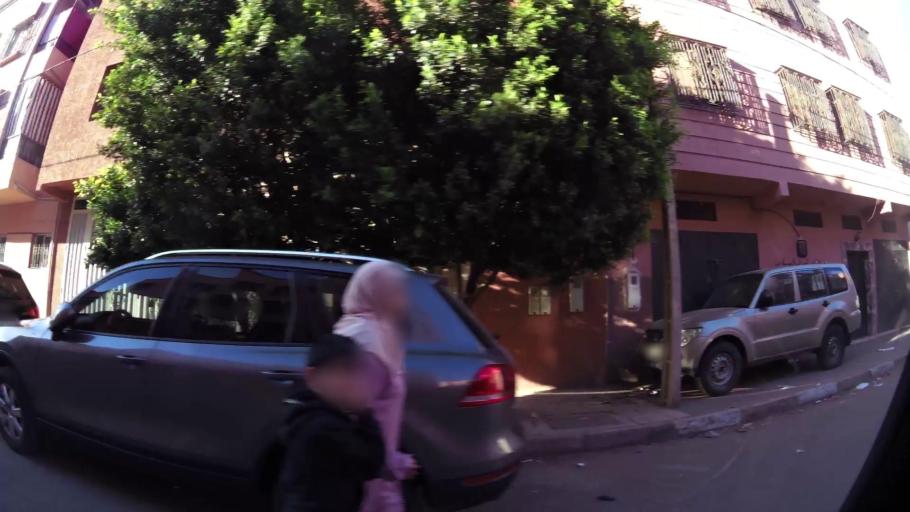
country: MA
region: Marrakech-Tensift-Al Haouz
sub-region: Marrakech
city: Marrakesh
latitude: 31.6199
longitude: -8.0627
